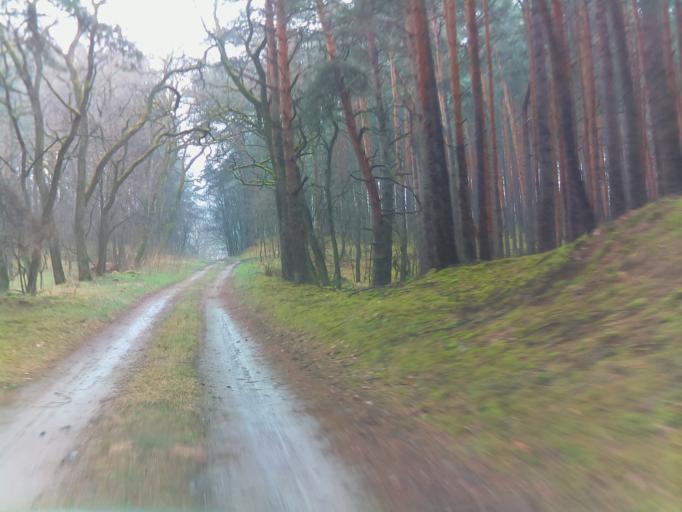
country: DE
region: Brandenburg
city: Jamlitz
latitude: 52.0431
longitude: 14.3649
